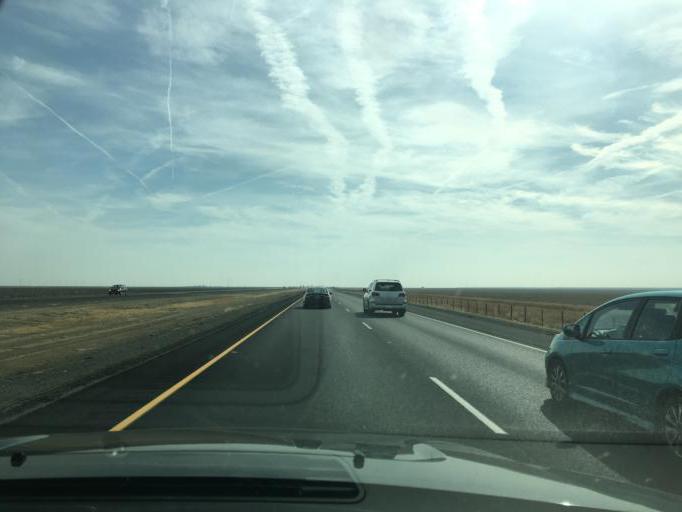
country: US
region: California
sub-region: Kern County
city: Lost Hills
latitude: 35.6979
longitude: -119.7141
